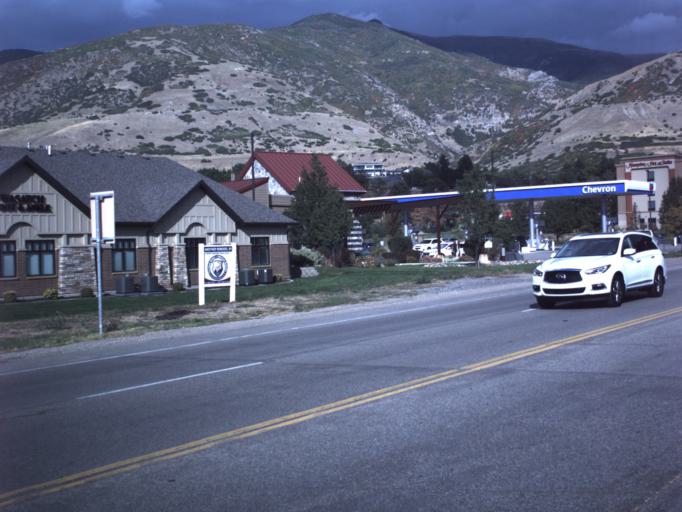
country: US
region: Utah
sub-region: Davis County
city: Farmington
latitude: 40.9914
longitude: -111.8981
